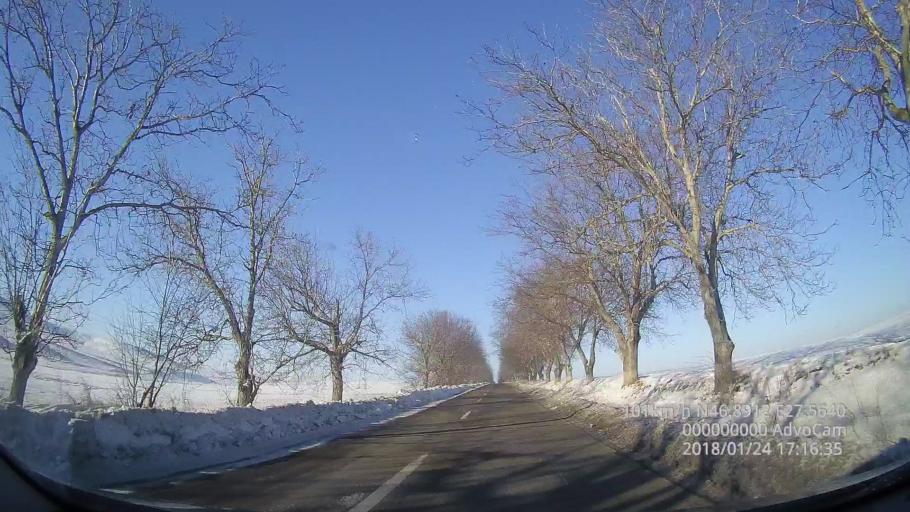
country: RO
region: Iasi
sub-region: Comuna Scanteia
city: Scanteia
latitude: 46.8920
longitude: 27.5640
